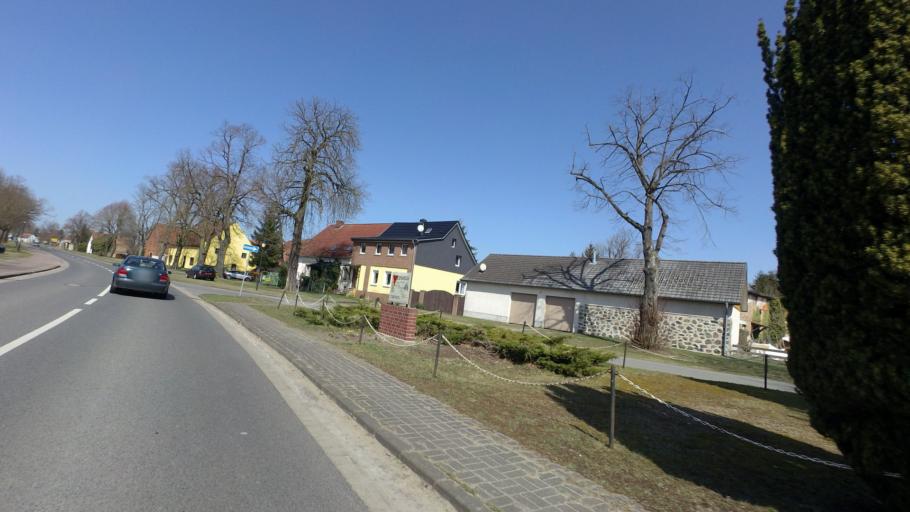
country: DE
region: Brandenburg
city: Lindow
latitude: 52.9332
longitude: 12.9713
